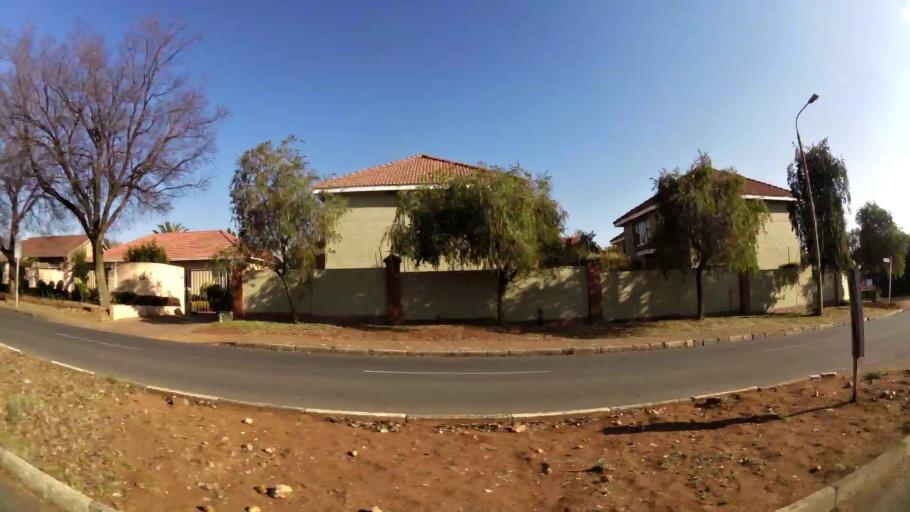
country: ZA
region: Gauteng
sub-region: City of Johannesburg Metropolitan Municipality
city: Modderfontein
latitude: -26.1503
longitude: 28.1631
